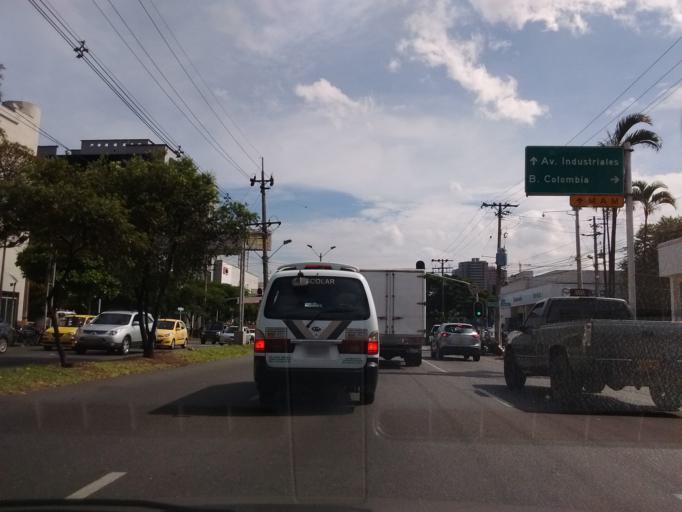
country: CO
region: Antioquia
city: Itagui
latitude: 6.2144
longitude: -75.5761
